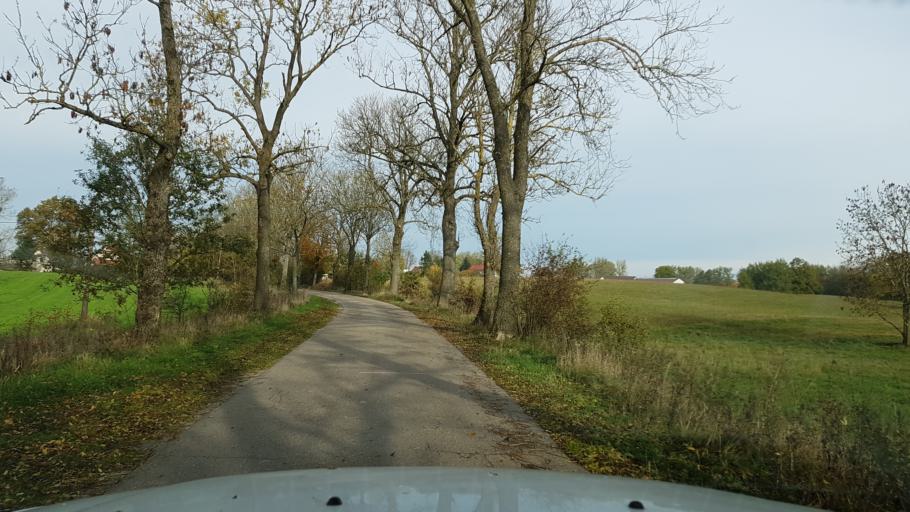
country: PL
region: West Pomeranian Voivodeship
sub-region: Powiat swidwinski
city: Polczyn-Zdroj
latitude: 53.7398
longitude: 16.0361
